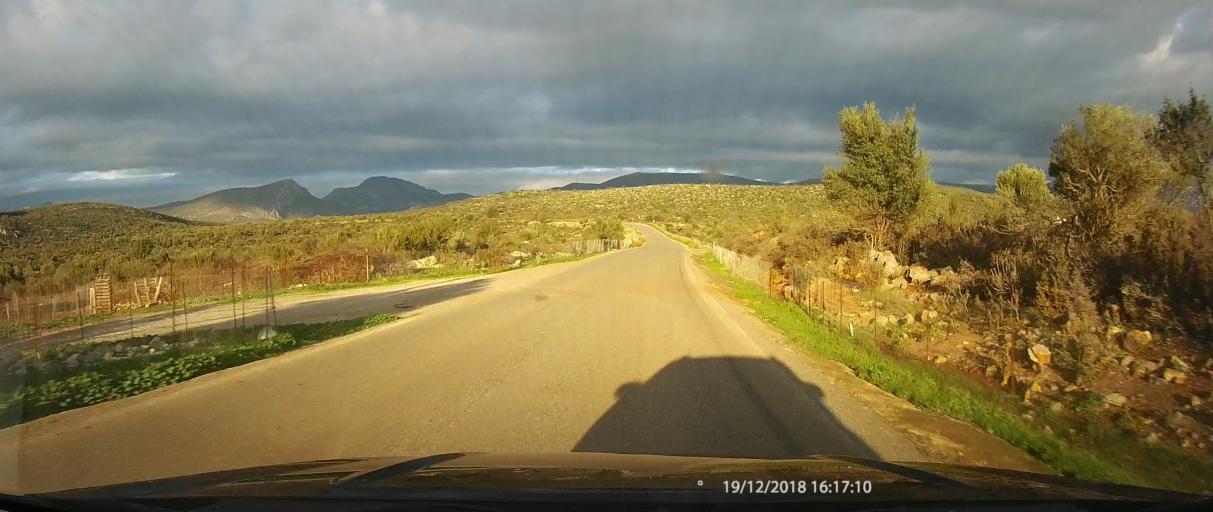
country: GR
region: Peloponnese
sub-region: Nomos Lakonias
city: Kato Glikovrisi
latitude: 36.9077
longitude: 22.8086
